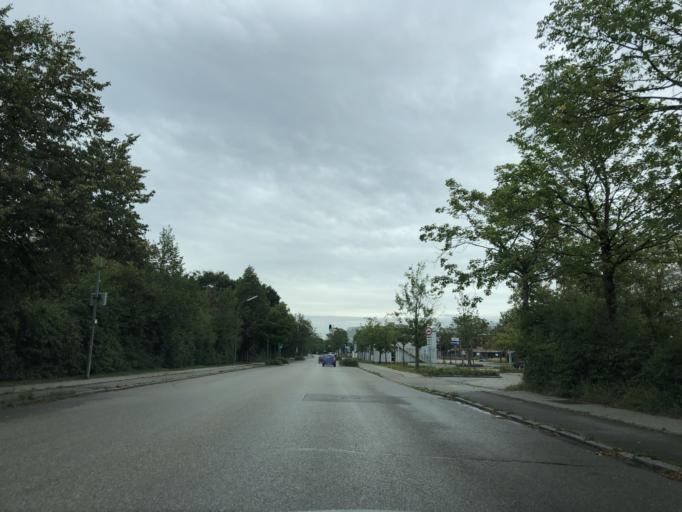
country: DE
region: Bavaria
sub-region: Upper Bavaria
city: Unterschleissheim
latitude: 48.2706
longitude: 11.5802
